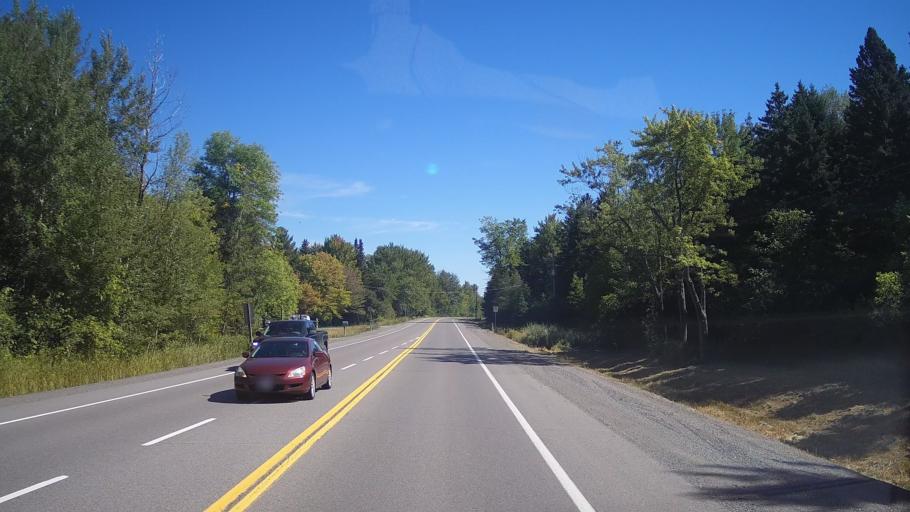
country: CA
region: Ontario
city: Bells Corners
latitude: 45.0611
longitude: -75.6712
